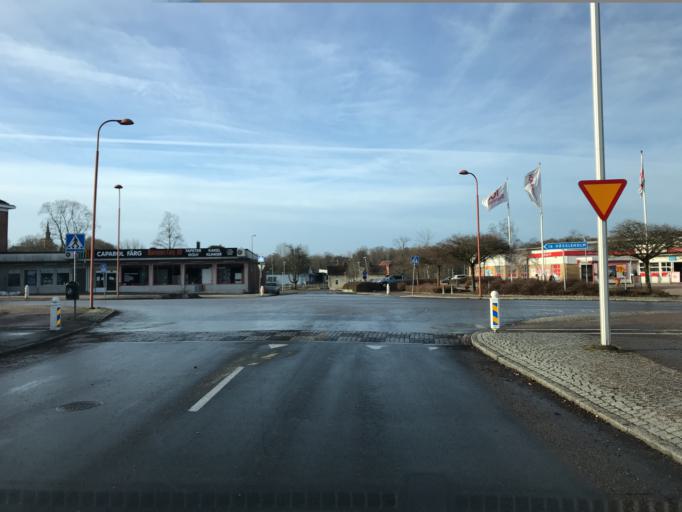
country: SE
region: Skane
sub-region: Hassleholms Kommun
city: Bjarnum
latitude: 56.2914
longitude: 13.7108
